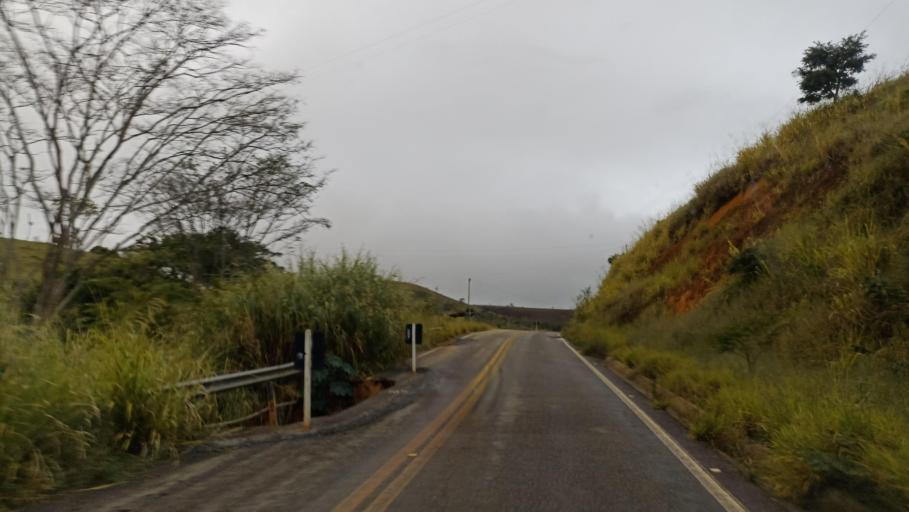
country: BR
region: Minas Gerais
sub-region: Joaima
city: Joaima
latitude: -16.6736
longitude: -40.5267
